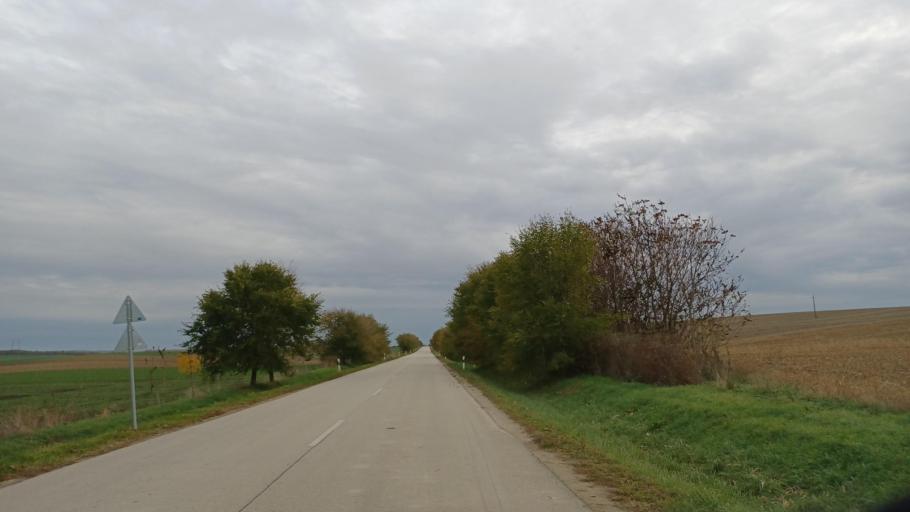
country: HU
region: Tolna
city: Nagydorog
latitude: 46.6796
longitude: 18.5997
